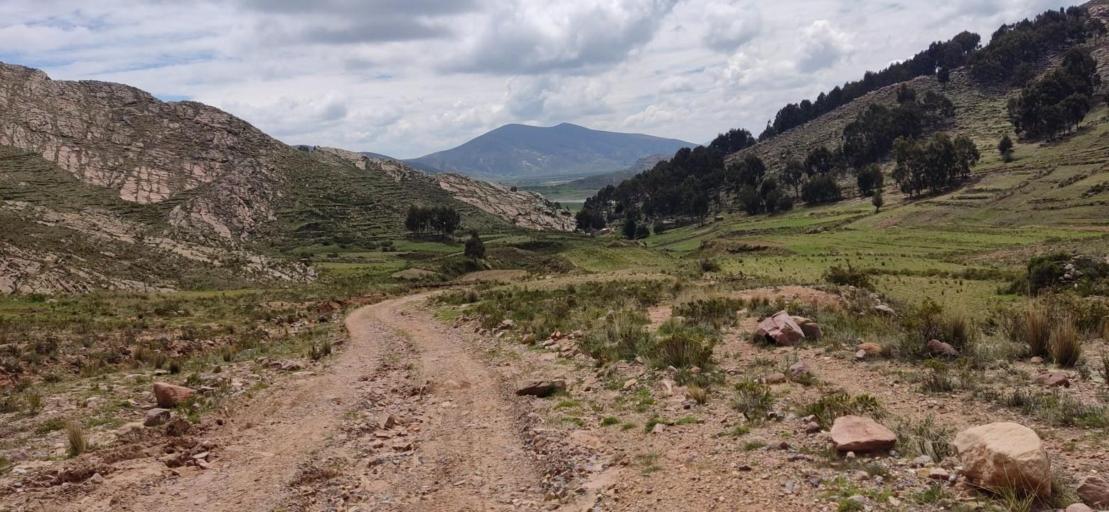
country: BO
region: La Paz
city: Batallas
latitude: -16.3443
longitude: -68.6474
